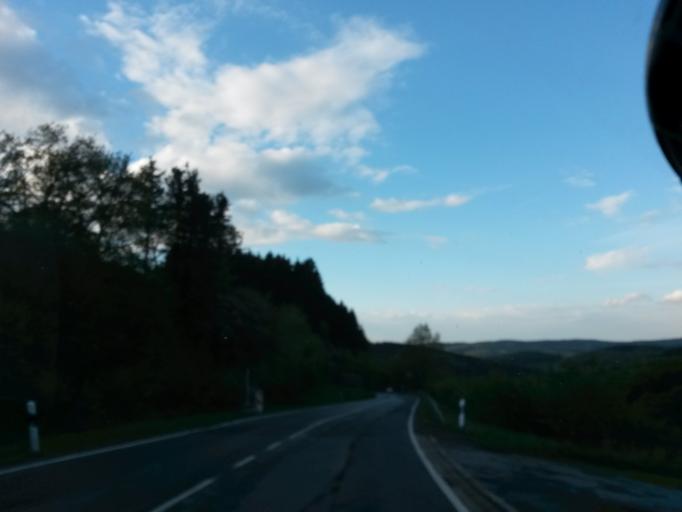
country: DE
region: North Rhine-Westphalia
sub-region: Regierungsbezirk Arnsberg
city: Herscheid
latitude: 51.1653
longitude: 7.7545
